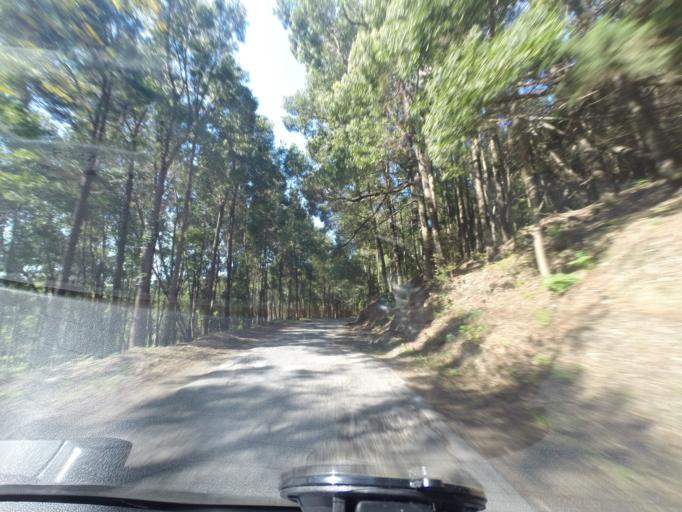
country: PT
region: Lisbon
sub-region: Sintra
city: Colares
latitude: 38.7703
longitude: -9.4368
